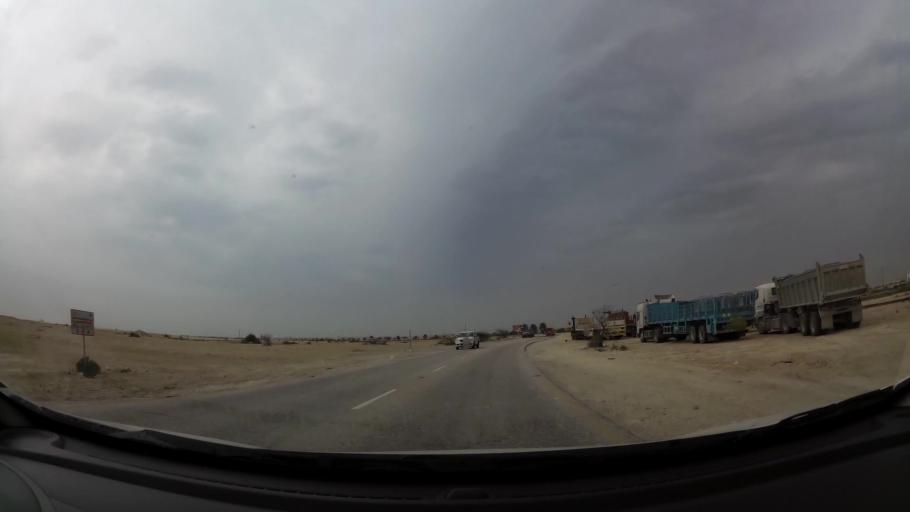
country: BH
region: Central Governorate
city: Dar Kulayb
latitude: 26.0779
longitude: 50.5443
